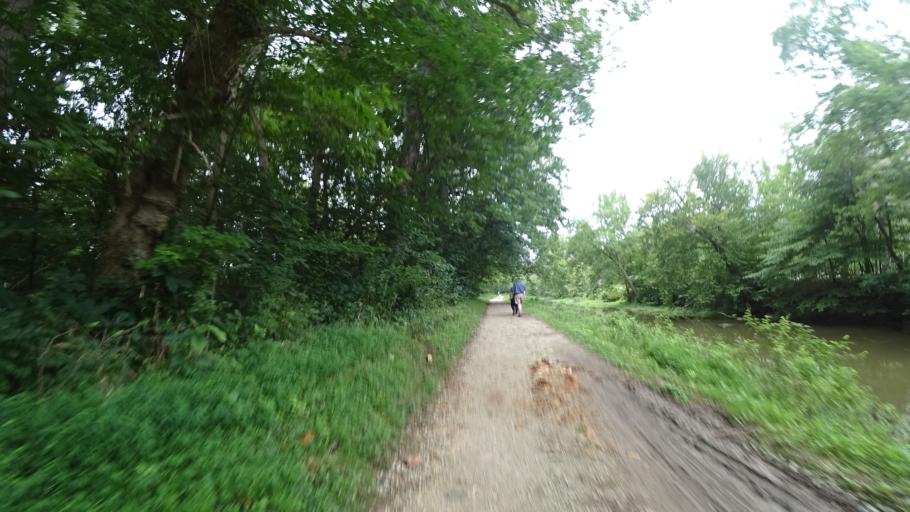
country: US
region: Maryland
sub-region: Montgomery County
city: Travilah
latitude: 39.0388
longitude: -77.2568
